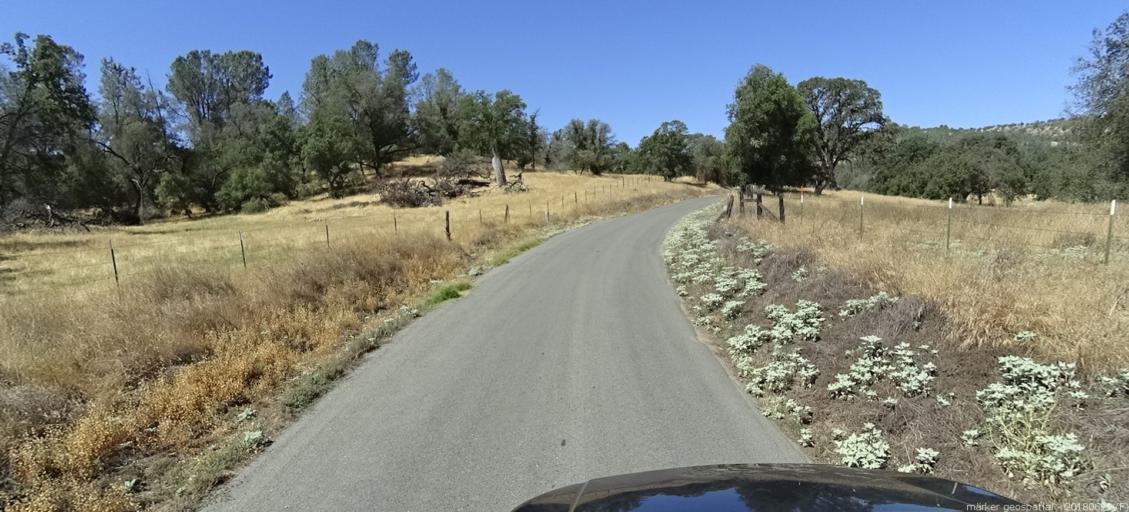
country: US
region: California
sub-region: Madera County
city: Yosemite Lakes
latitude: 37.1313
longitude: -119.7569
